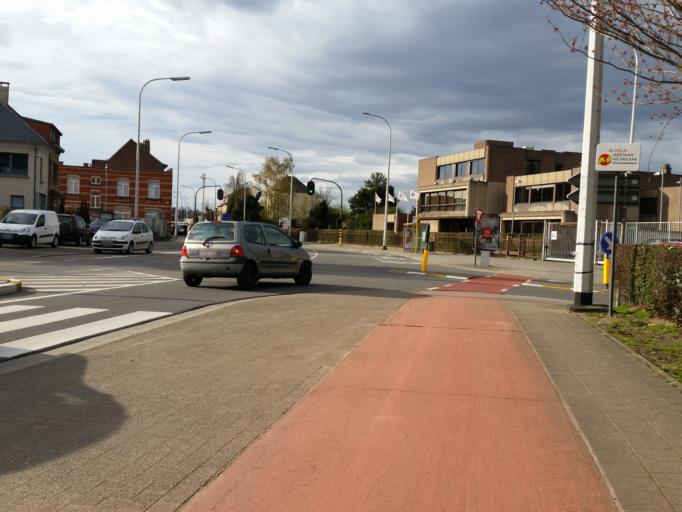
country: BE
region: Flanders
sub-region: Provincie Vlaams-Brabant
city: Dilbeek
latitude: 50.8761
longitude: 4.2847
